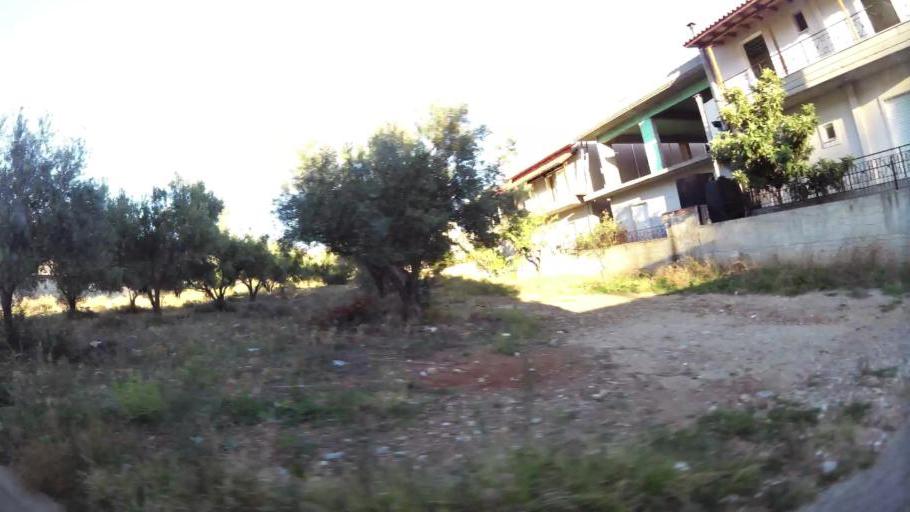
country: GR
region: Attica
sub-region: Nomarchia Dytikis Attikis
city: Ano Liosia
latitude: 38.1026
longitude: 23.7142
